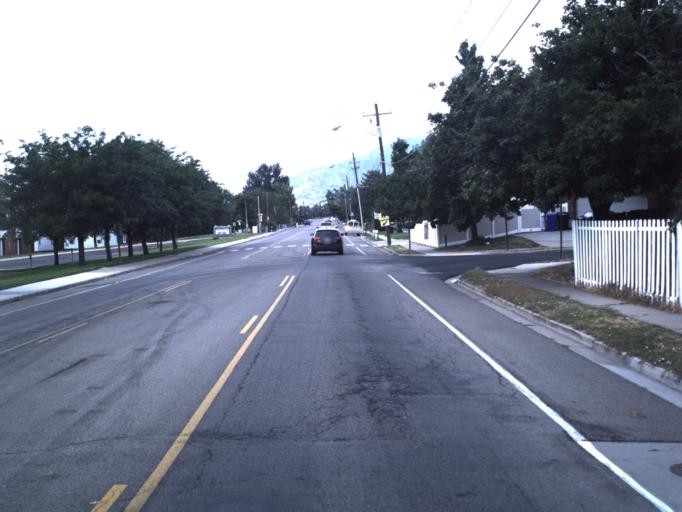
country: US
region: Utah
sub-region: Davis County
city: Centerville
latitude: 40.9302
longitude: -111.8789
